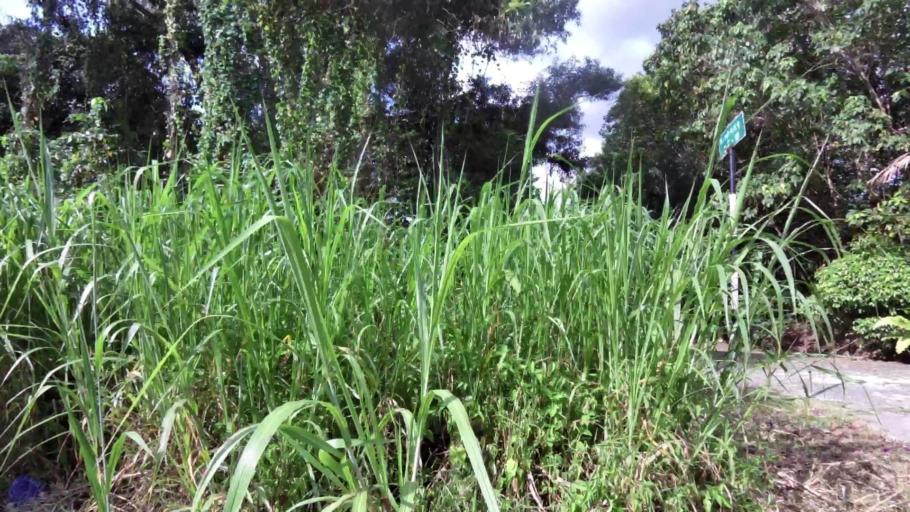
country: BN
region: Brunei and Muara
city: Bandar Seri Begawan
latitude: 4.9545
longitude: 114.9693
